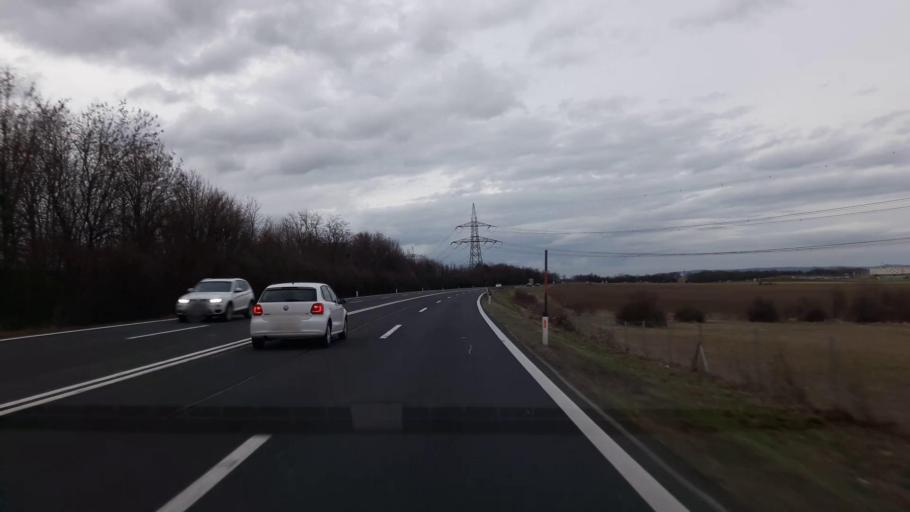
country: AT
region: Burgenland
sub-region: Politischer Bezirk Mattersburg
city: Mattersburg
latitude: 47.7350
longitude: 16.3719
